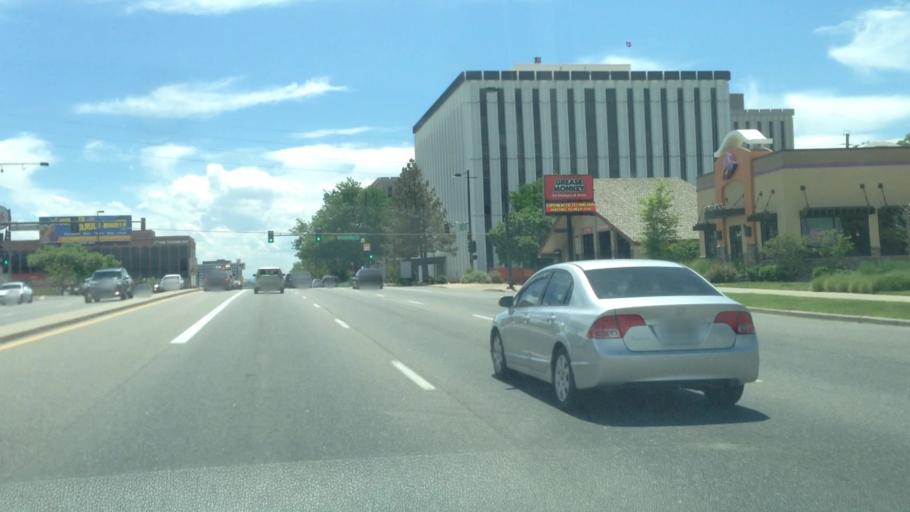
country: US
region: Colorado
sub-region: Arapahoe County
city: Glendale
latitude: 39.6938
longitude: -104.9407
